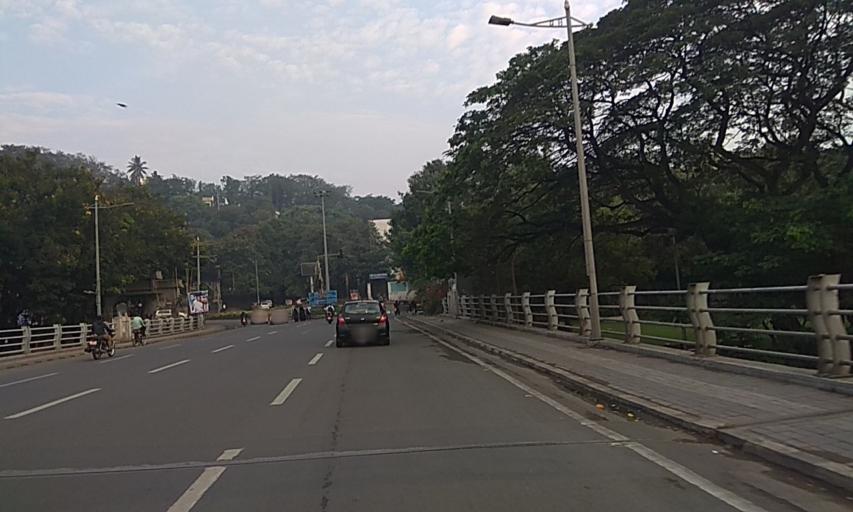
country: IN
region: Maharashtra
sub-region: Pune Division
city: Shivaji Nagar
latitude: 18.5442
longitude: 73.8835
